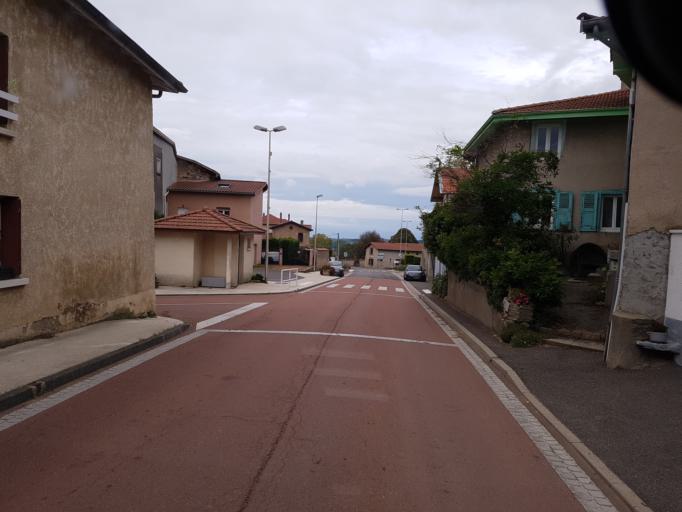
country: FR
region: Rhone-Alpes
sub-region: Departement de la Loire
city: Chazelles-sur-Lyon
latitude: 45.6565
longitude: 4.4194
